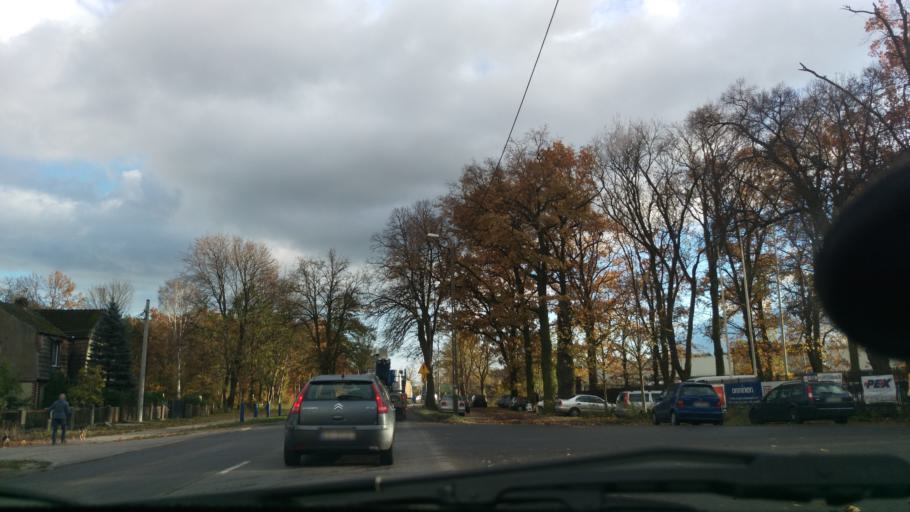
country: PL
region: West Pomeranian Voivodeship
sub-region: Szczecin
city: Szczecin
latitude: 53.3843
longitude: 14.6805
